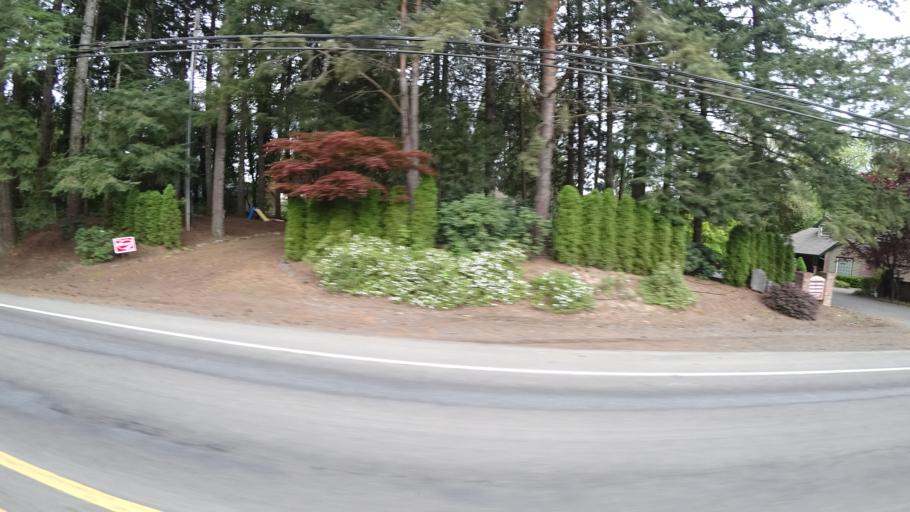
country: US
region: Oregon
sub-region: Washington County
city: Hillsboro
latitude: 45.5456
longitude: -122.9797
